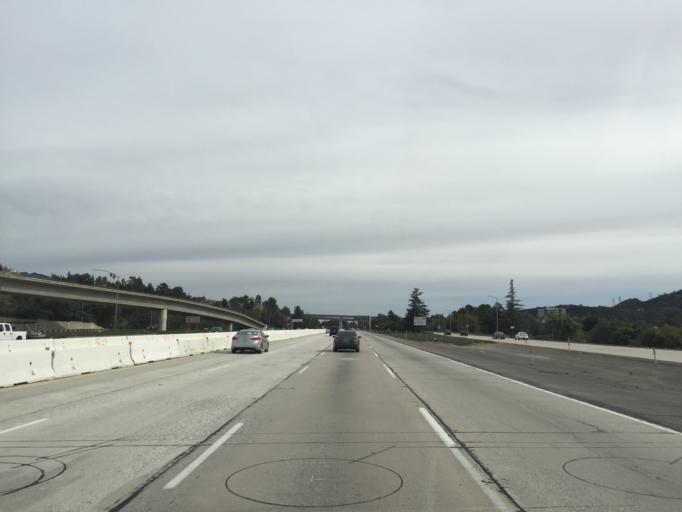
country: US
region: California
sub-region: Los Angeles County
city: La Crescenta-Montrose
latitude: 34.2107
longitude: -118.2256
